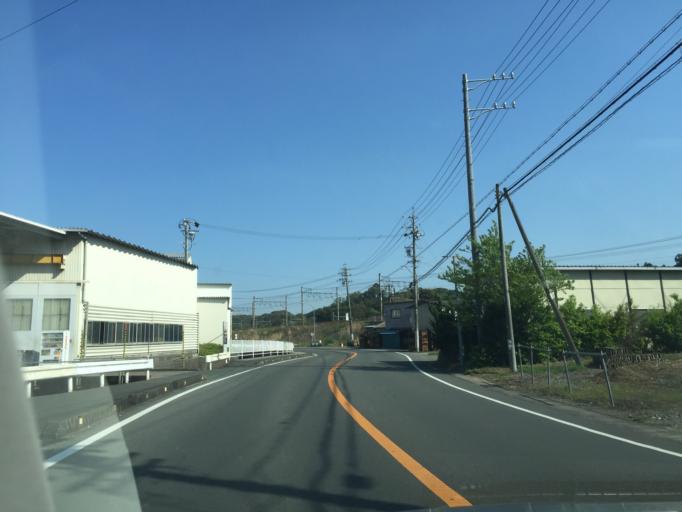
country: JP
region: Shizuoka
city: Kakegawa
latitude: 34.7768
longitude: 138.0391
